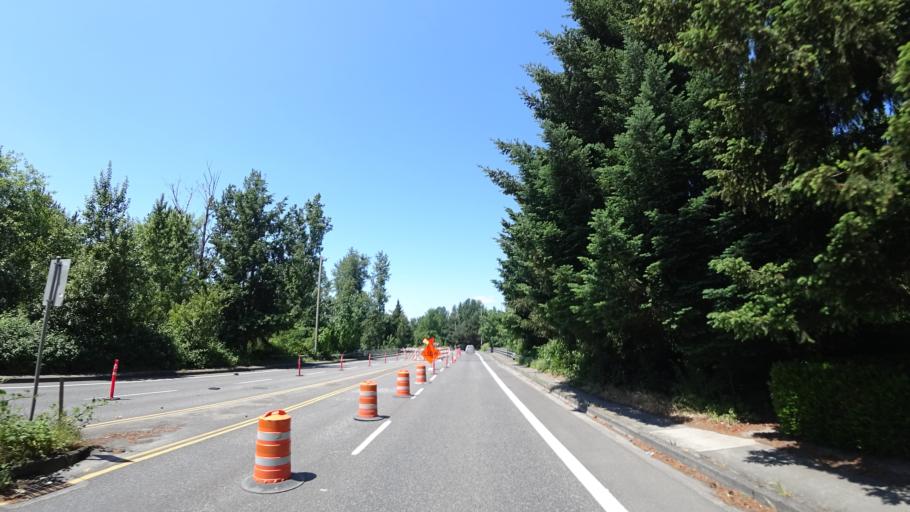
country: US
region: Oregon
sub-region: Multnomah County
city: Fairview
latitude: 45.5545
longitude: -122.4903
